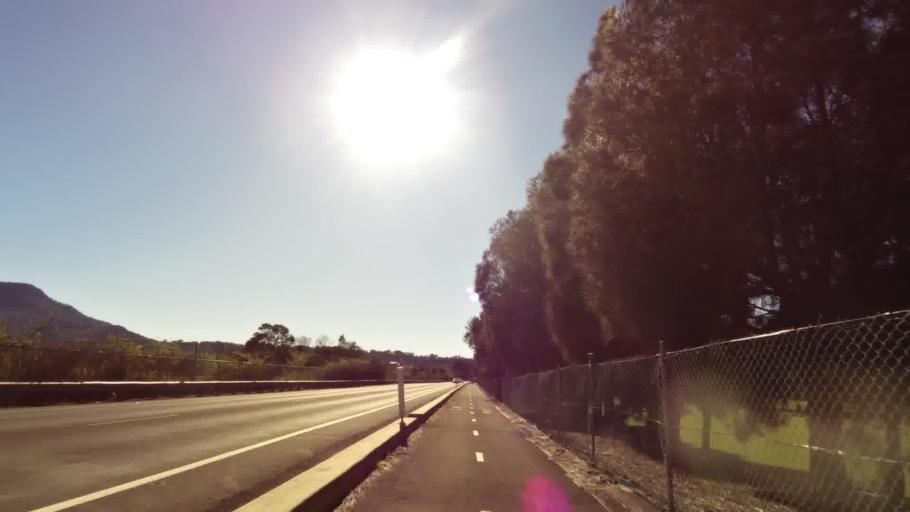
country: AU
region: New South Wales
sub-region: Wollongong
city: Koonawarra
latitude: -34.4784
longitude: 150.8066
